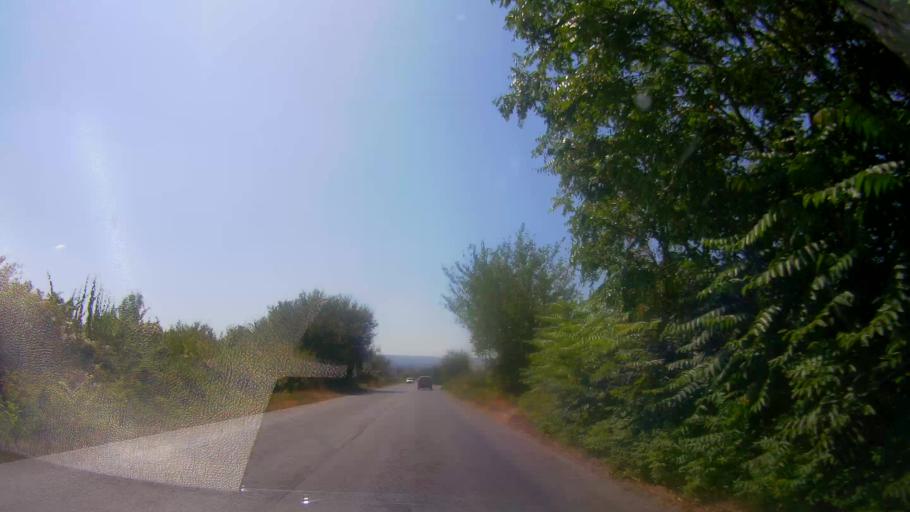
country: BG
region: Veliko Turnovo
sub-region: Obshtina Gorna Oryakhovitsa
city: Purvomaytsi
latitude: 43.2269
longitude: 25.6386
